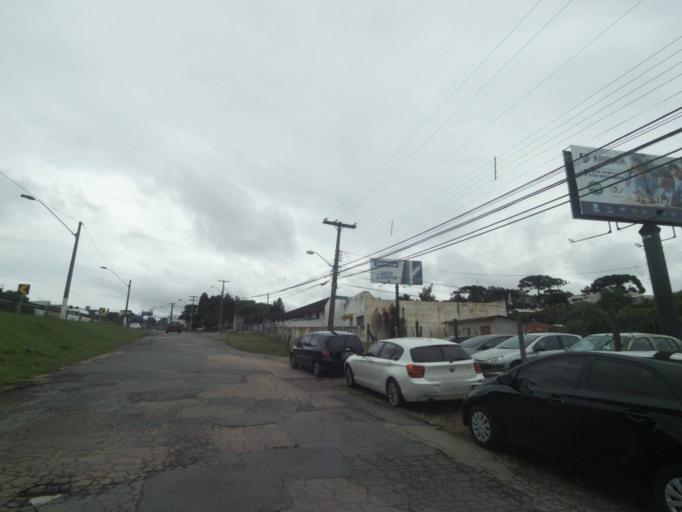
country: BR
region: Parana
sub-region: Curitiba
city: Curitiba
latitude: -25.4298
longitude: -49.3201
